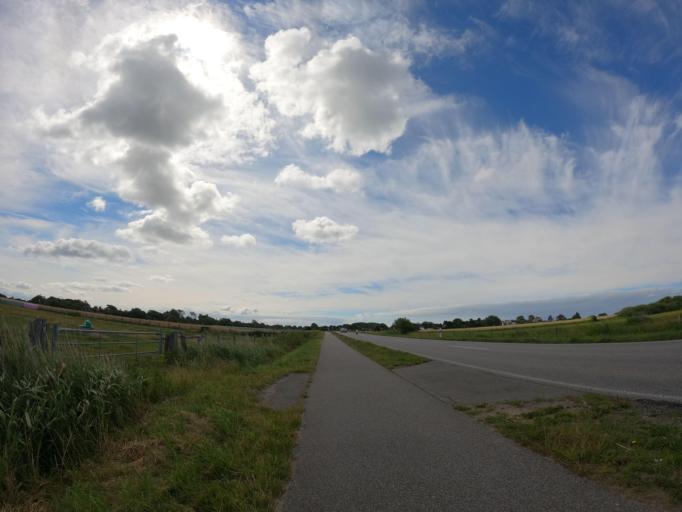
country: DE
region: Schleswig-Holstein
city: Sylt-Ost
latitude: 54.8774
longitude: 8.3917
